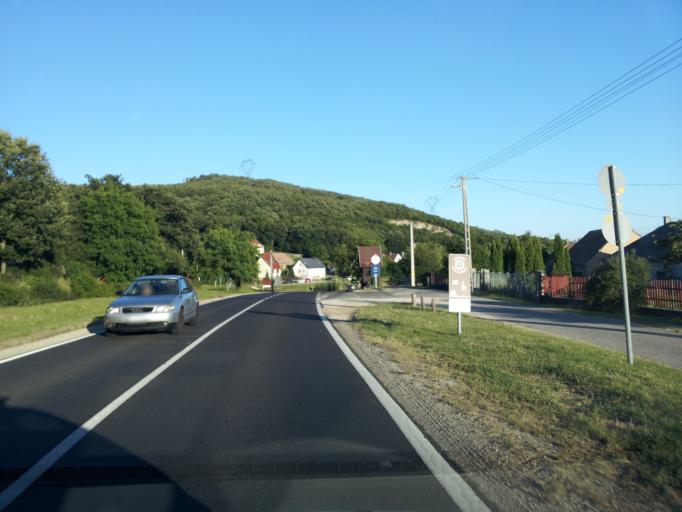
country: HU
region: Veszprem
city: Zirc
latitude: 47.2067
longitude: 17.9193
